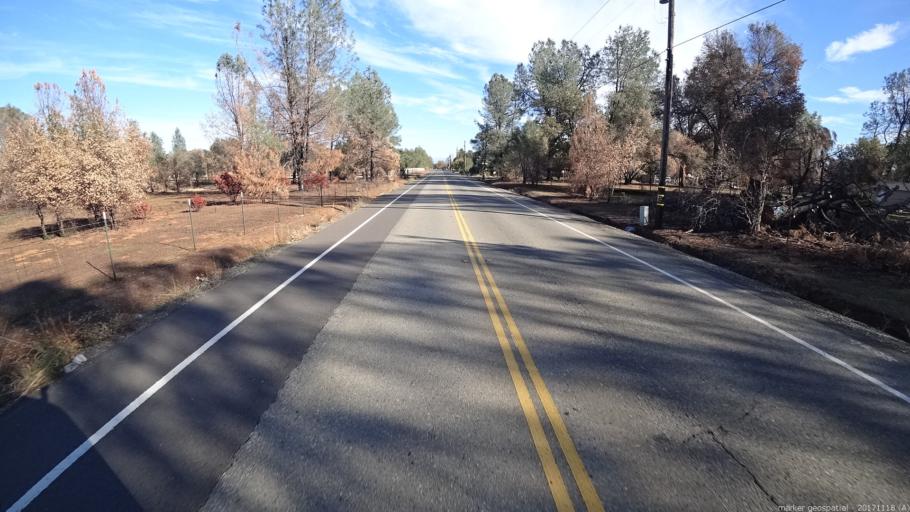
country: US
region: California
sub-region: Shasta County
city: Redding
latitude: 40.4781
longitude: -122.4368
